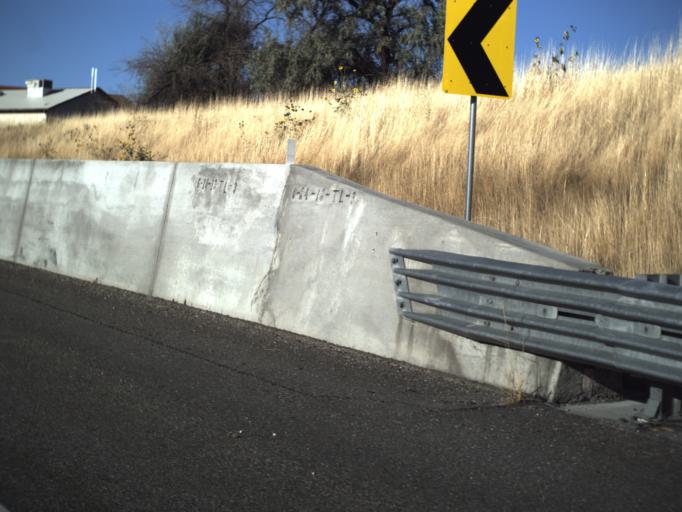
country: US
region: Utah
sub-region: Weber County
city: Riverdale
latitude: 41.1869
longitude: -112.0104
